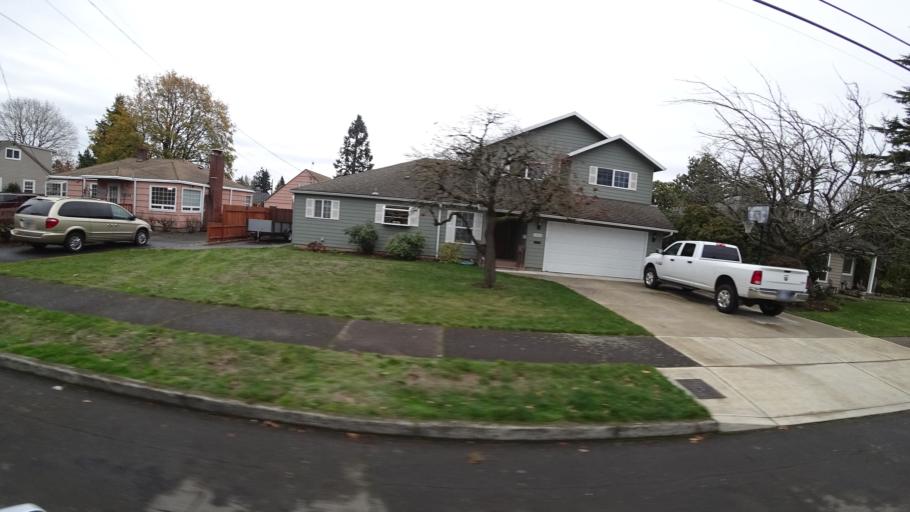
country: US
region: Oregon
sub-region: Multnomah County
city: Lents
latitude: 45.5290
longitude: -122.5546
